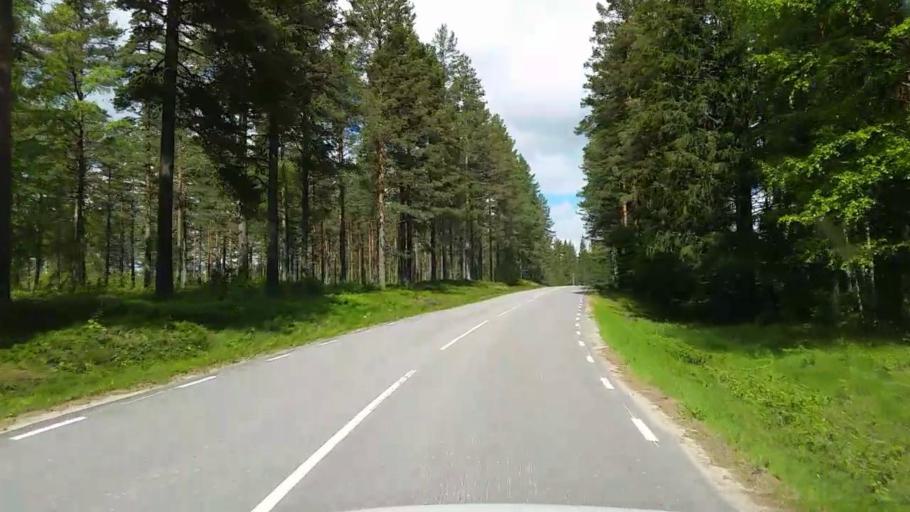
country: SE
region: Gaevleborg
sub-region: Bollnas Kommun
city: Vittsjo
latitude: 61.1302
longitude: 16.1755
